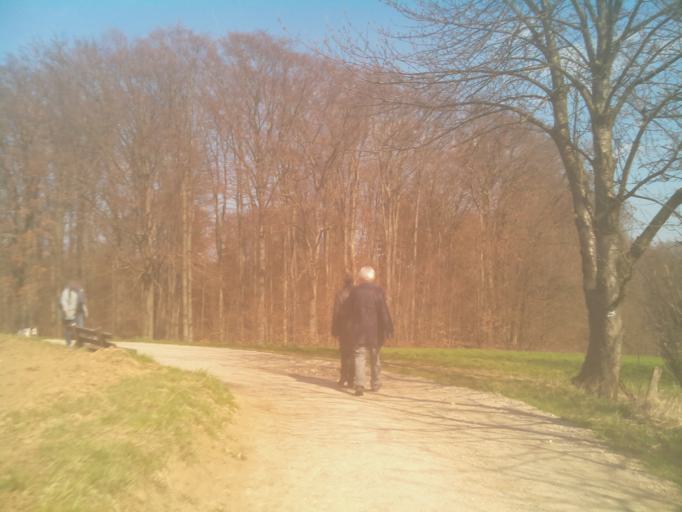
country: DE
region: Hesse
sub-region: Regierungsbezirk Darmstadt
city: Morlenbach
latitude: 49.5897
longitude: 8.7115
